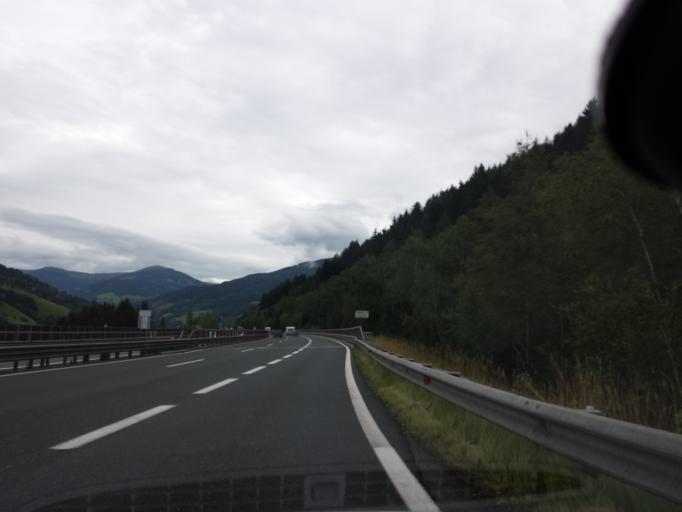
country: AT
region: Carinthia
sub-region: Politischer Bezirk Spittal an der Drau
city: Gmuend
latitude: 46.9215
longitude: 13.5812
